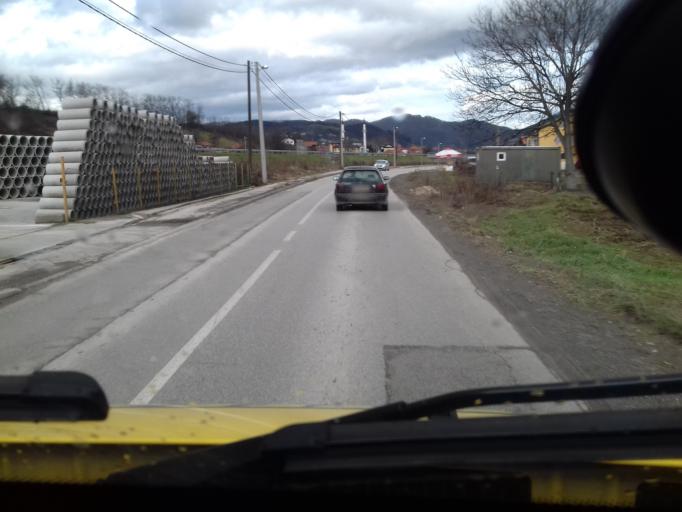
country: BA
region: Federation of Bosnia and Herzegovina
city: Gornje Mostre
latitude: 44.0216
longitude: 18.1360
